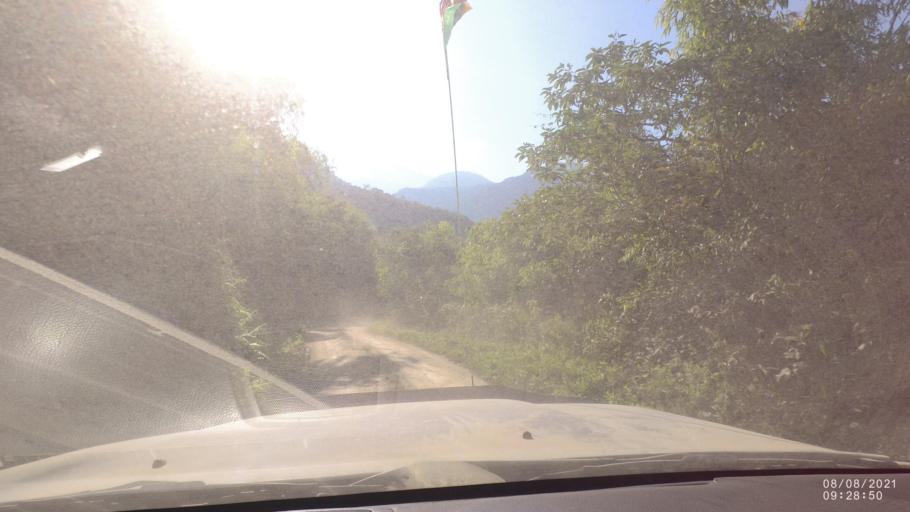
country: BO
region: La Paz
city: Quime
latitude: -16.5864
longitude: -66.7138
